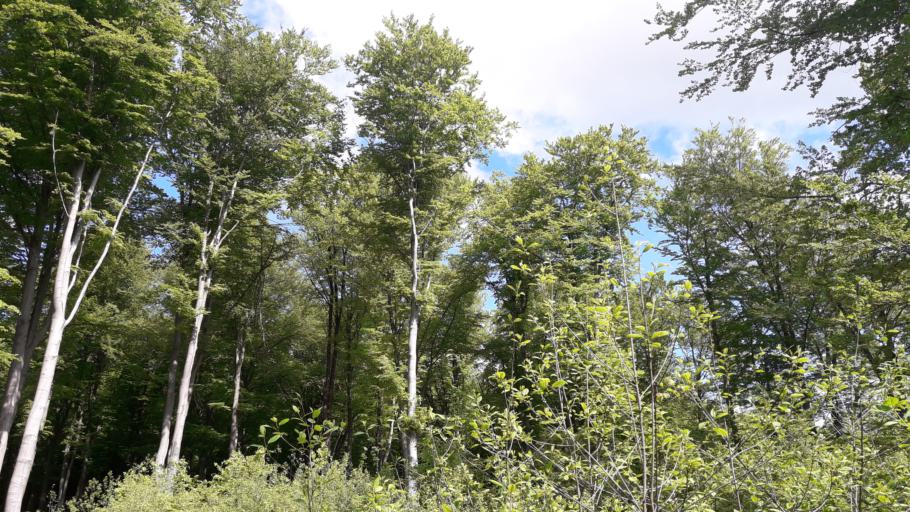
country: PL
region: Subcarpathian Voivodeship
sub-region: Powiat przeworski
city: Manasterz
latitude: 49.9466
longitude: 22.3101
